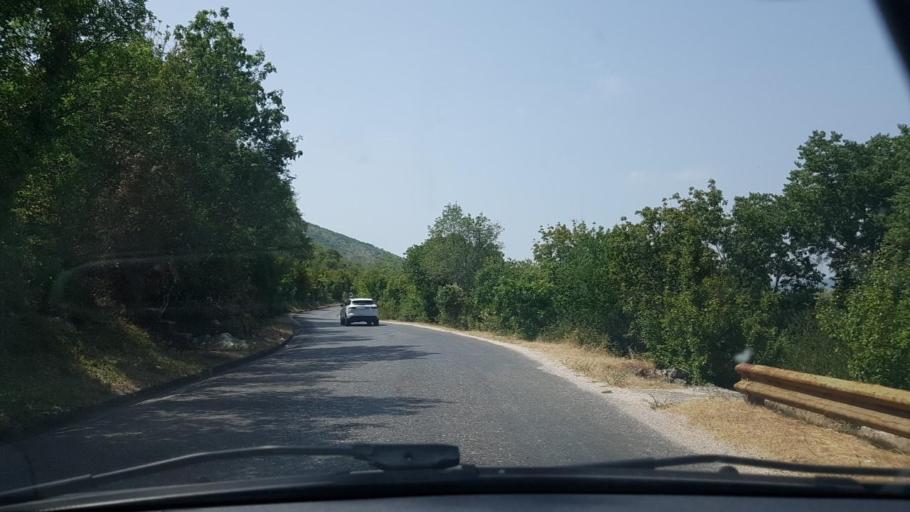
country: BA
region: Federation of Bosnia and Herzegovina
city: Tasovcici
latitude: 43.0356
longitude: 17.7244
